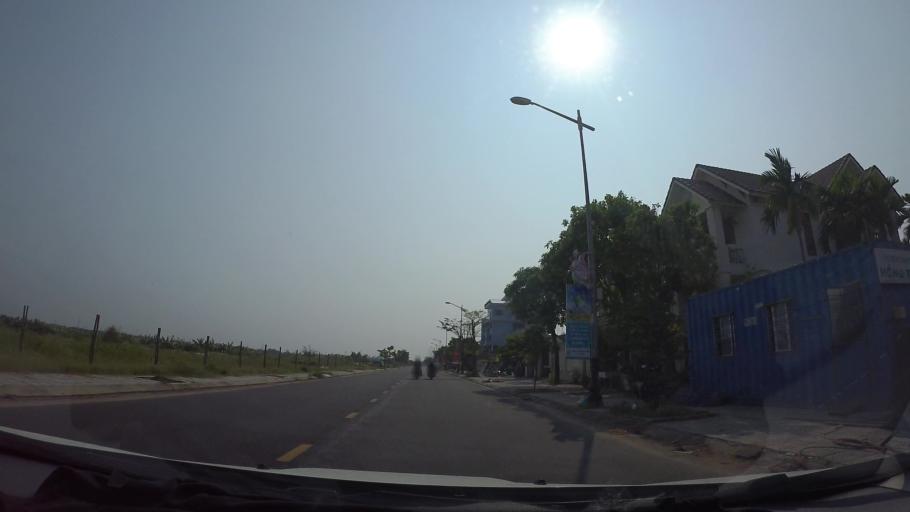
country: VN
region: Da Nang
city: Cam Le
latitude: 16.0070
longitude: 108.1996
